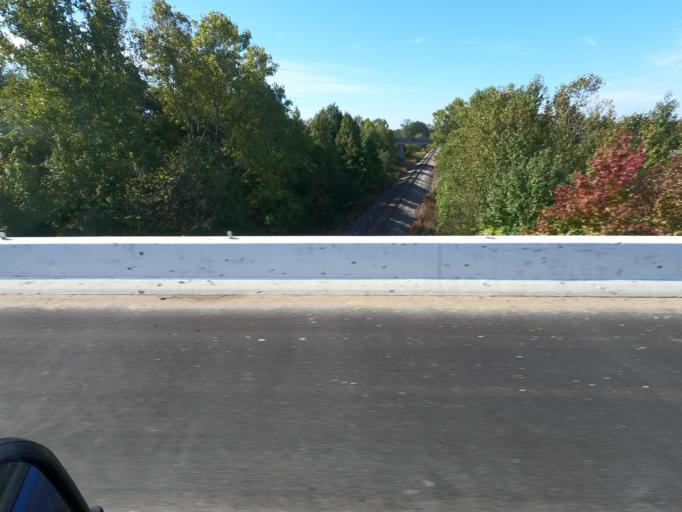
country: US
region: Tennessee
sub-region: Shelby County
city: Arlington
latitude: 35.2874
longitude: -89.6851
